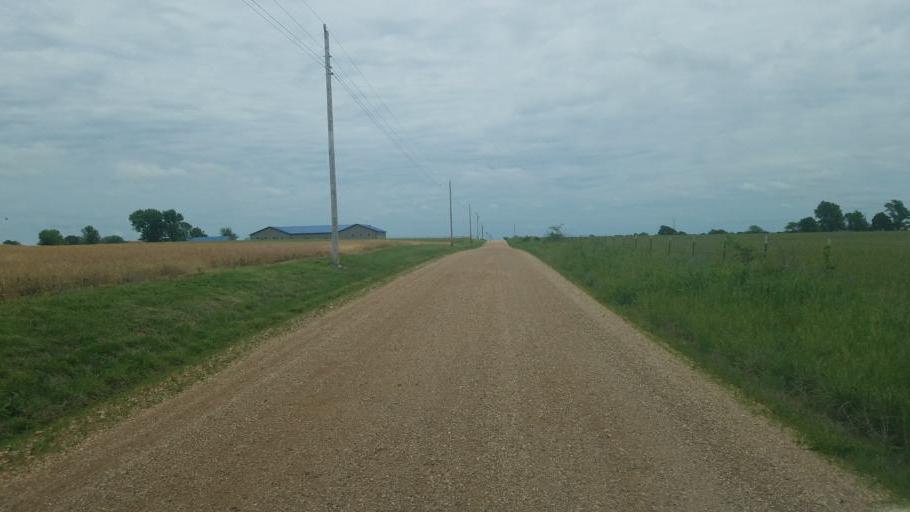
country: US
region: Missouri
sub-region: Morgan County
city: Versailles
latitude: 38.4929
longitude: -92.7941
